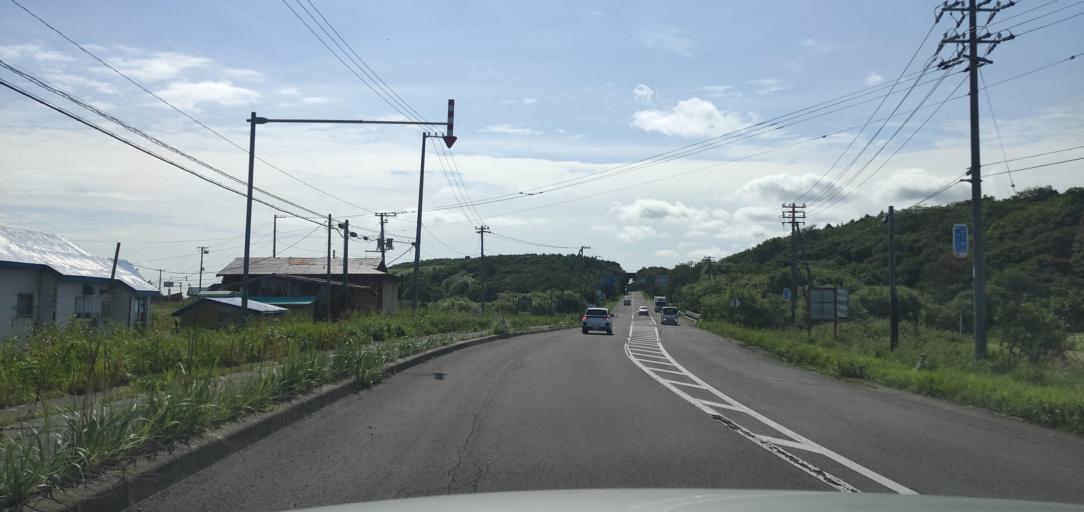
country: JP
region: Hokkaido
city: Shibetsu
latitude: 43.6394
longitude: 145.1620
